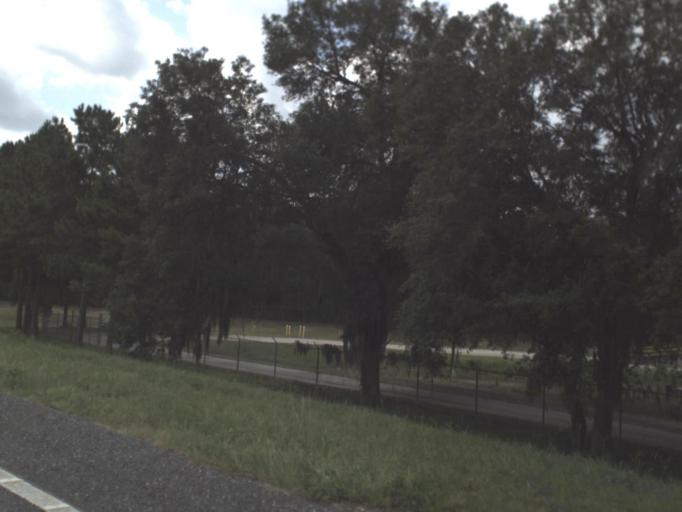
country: US
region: Florida
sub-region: Hernando County
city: Ridge Manor
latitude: 28.5091
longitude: -82.2021
